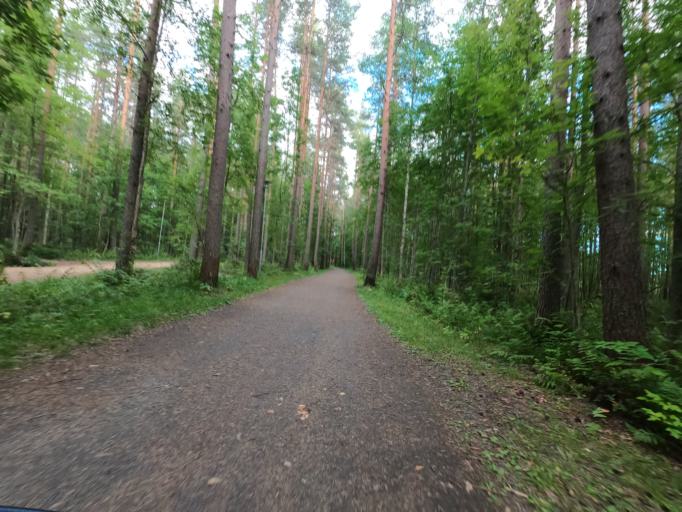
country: FI
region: North Karelia
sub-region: Joensuu
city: Joensuu
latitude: 62.6038
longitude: 29.7346
